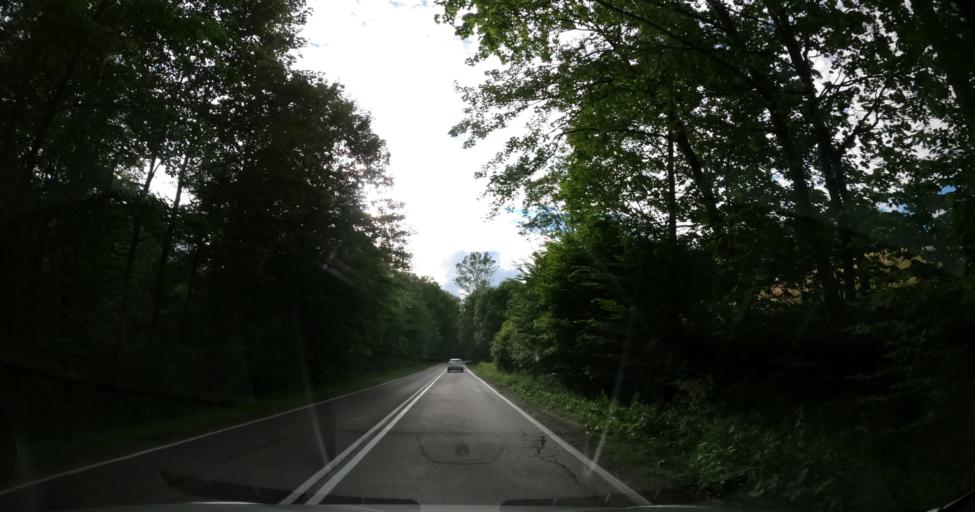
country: PL
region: Pomeranian Voivodeship
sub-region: Powiat kartuski
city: Sierakowice
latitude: 54.3413
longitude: 17.9477
